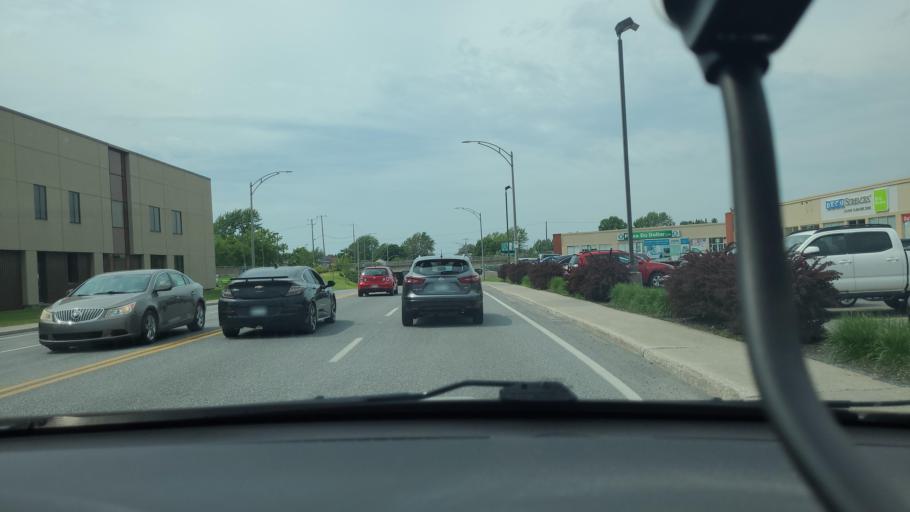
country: CA
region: Quebec
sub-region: Monteregie
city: Saint-Hyacinthe
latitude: 45.6236
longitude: -72.9601
